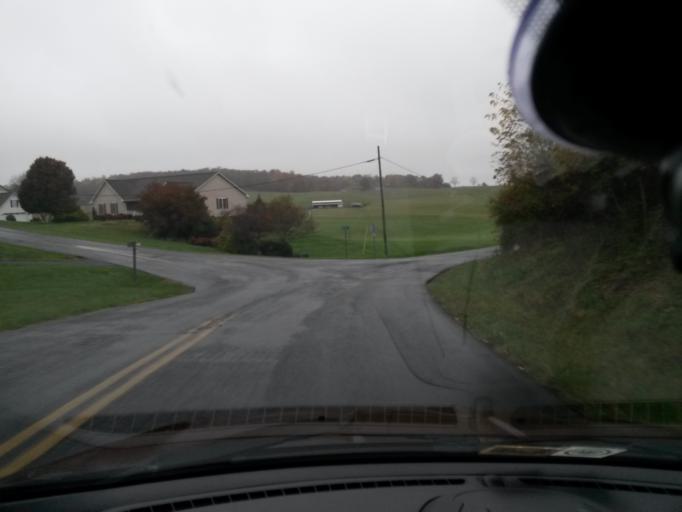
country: US
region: Virginia
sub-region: Botetourt County
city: Fincastle
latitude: 37.4746
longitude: -79.8484
